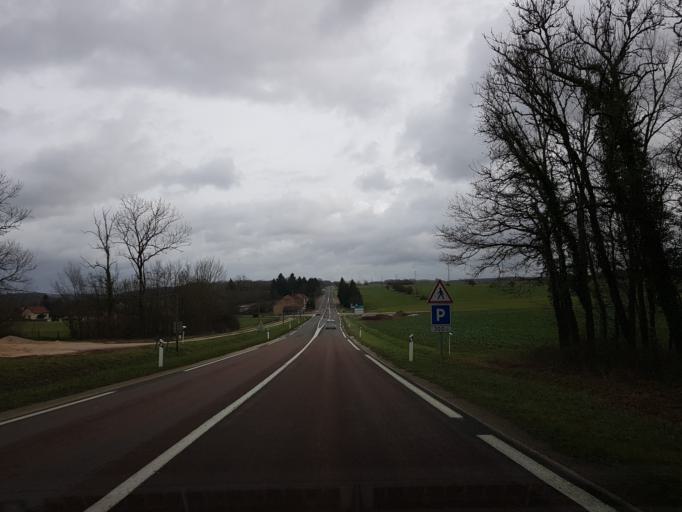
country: FR
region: Champagne-Ardenne
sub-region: Departement de la Haute-Marne
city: Chalindrey
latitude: 47.8181
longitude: 5.4881
